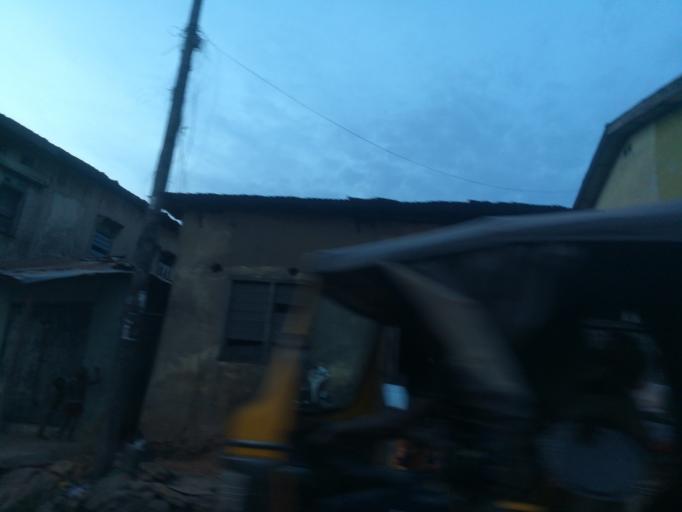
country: NG
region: Oyo
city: Ibadan
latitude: 7.3787
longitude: 3.8989
